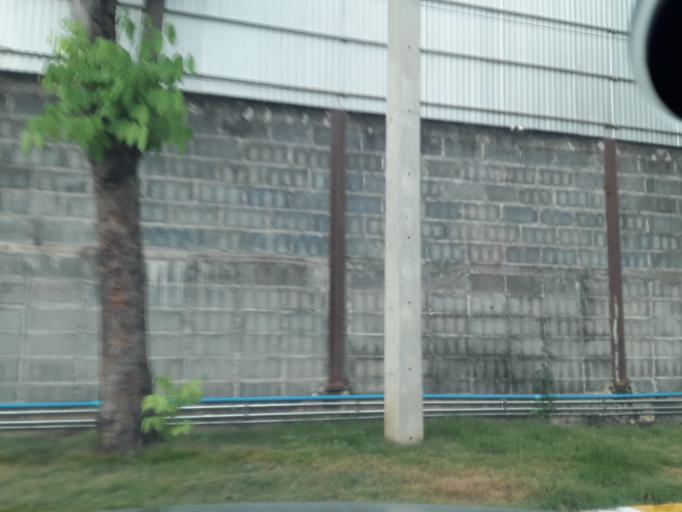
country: TH
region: Phra Nakhon Si Ayutthaya
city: Wang Noi
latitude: 14.2446
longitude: 100.7489
